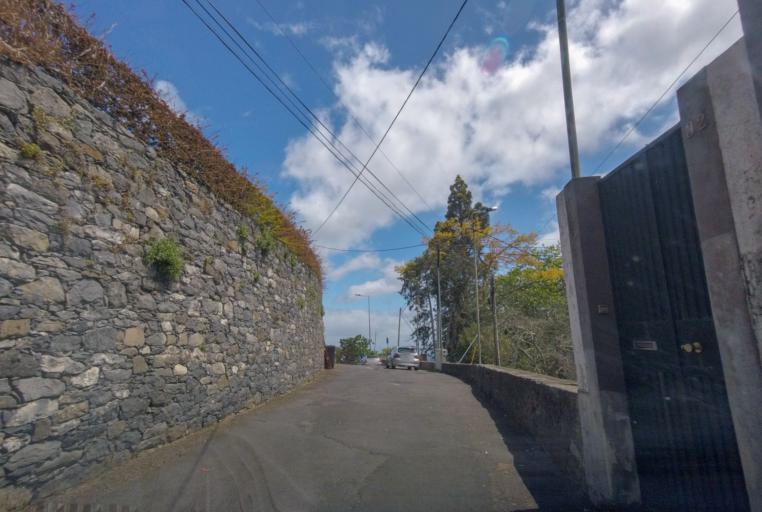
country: PT
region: Madeira
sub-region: Funchal
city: Nossa Senhora do Monte
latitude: 32.6774
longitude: -16.9021
